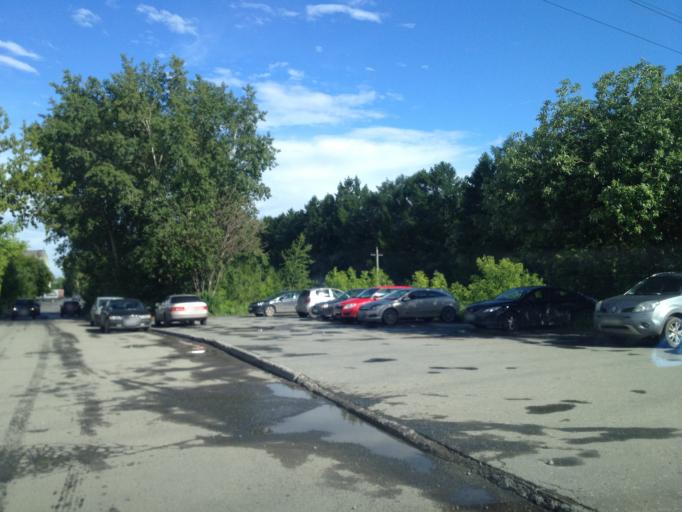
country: RU
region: Sverdlovsk
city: Yekaterinburg
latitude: 56.8182
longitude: 60.6727
